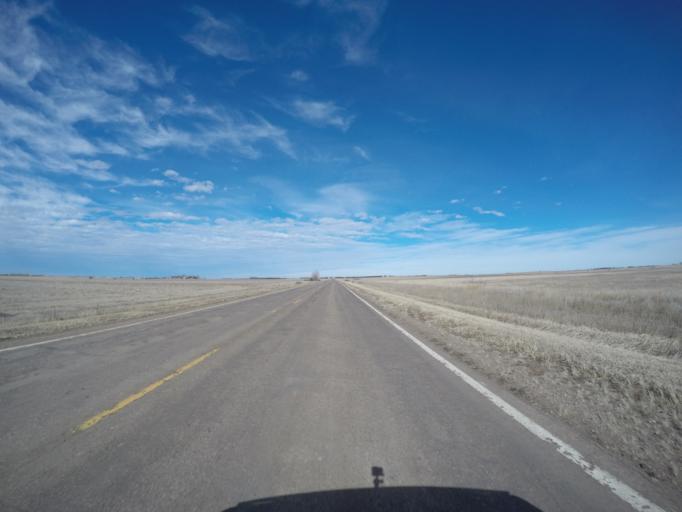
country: US
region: Nebraska
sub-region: Franklin County
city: Franklin
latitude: 40.1821
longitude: -98.9526
